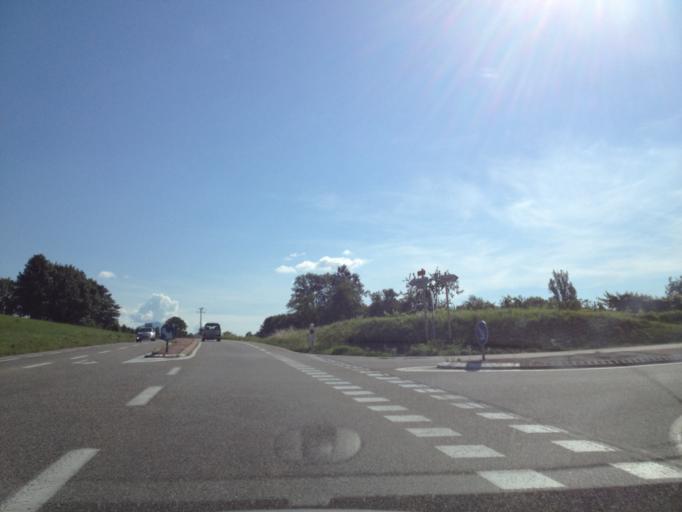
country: FR
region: Rhone-Alpes
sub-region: Departement de la Savoie
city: Sonnaz
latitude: 45.6250
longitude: 5.9124
